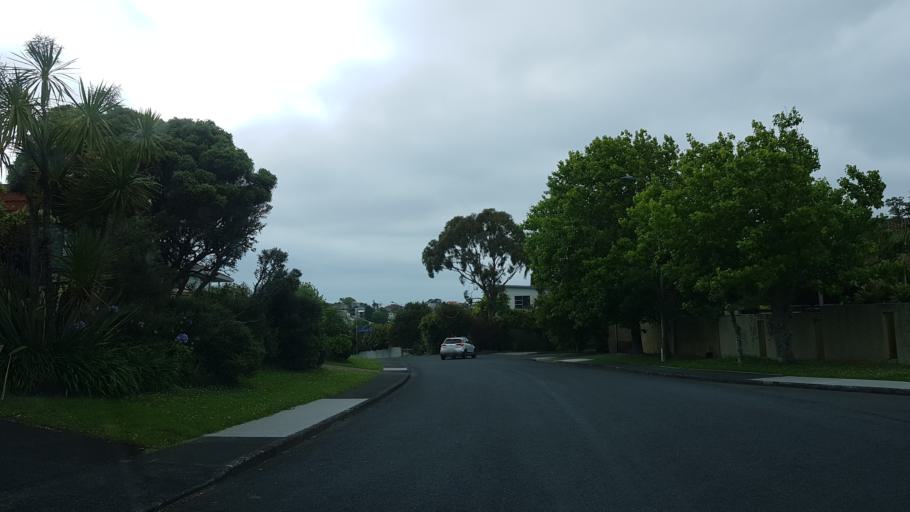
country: NZ
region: Auckland
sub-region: Auckland
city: North Shore
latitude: -36.8082
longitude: 174.7470
